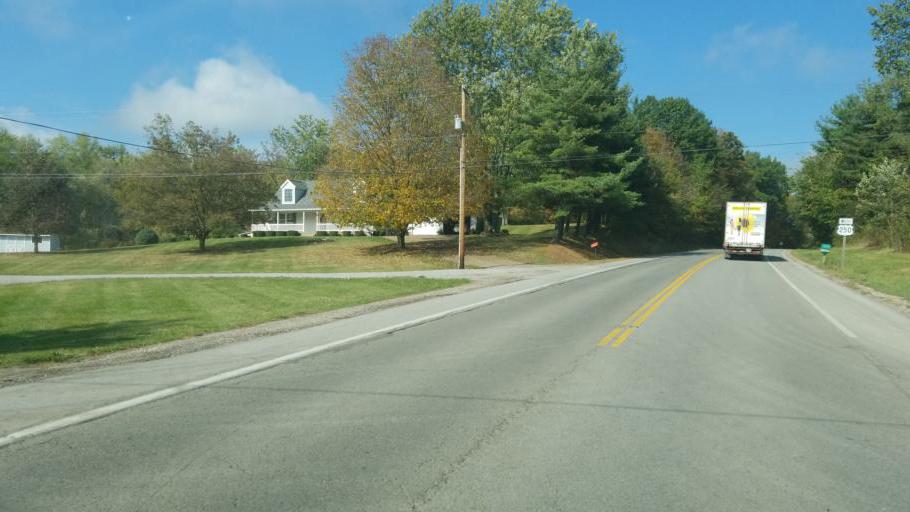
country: US
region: Ohio
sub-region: Stark County
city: Brewster
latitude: 40.6770
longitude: -81.6661
